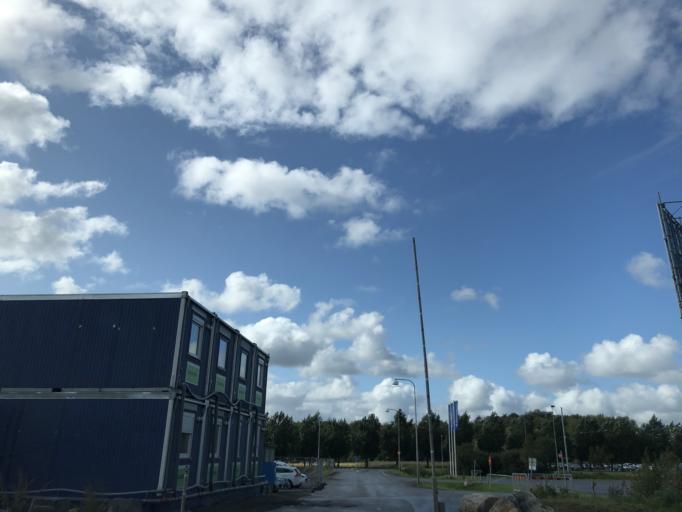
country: SE
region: Vaestra Goetaland
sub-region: Goteborg
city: Majorna
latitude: 57.7154
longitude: 11.8496
